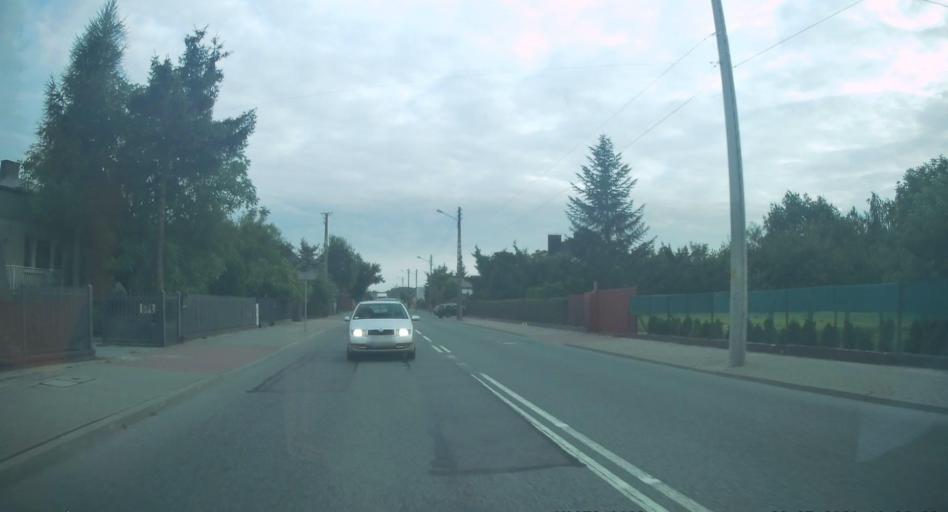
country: PL
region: Lodz Voivodeship
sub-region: Powiat radomszczanski
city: Kamiensk
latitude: 51.1986
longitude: 19.4995
